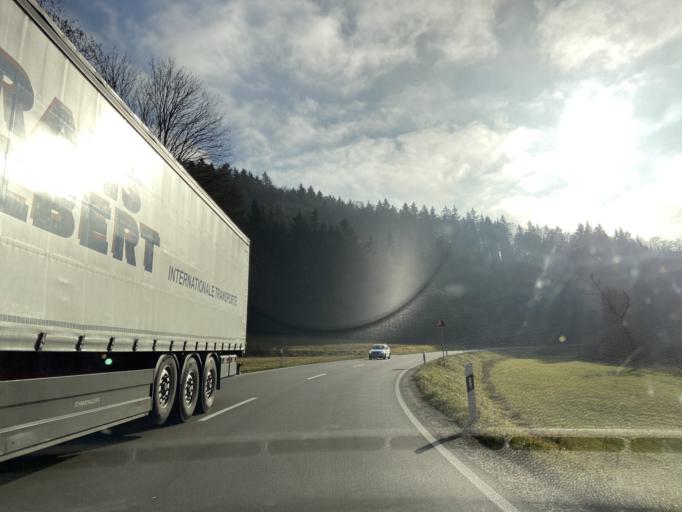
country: DE
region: Baden-Wuerttemberg
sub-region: Tuebingen Region
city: Veringenstadt
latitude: 48.1960
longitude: 9.2215
